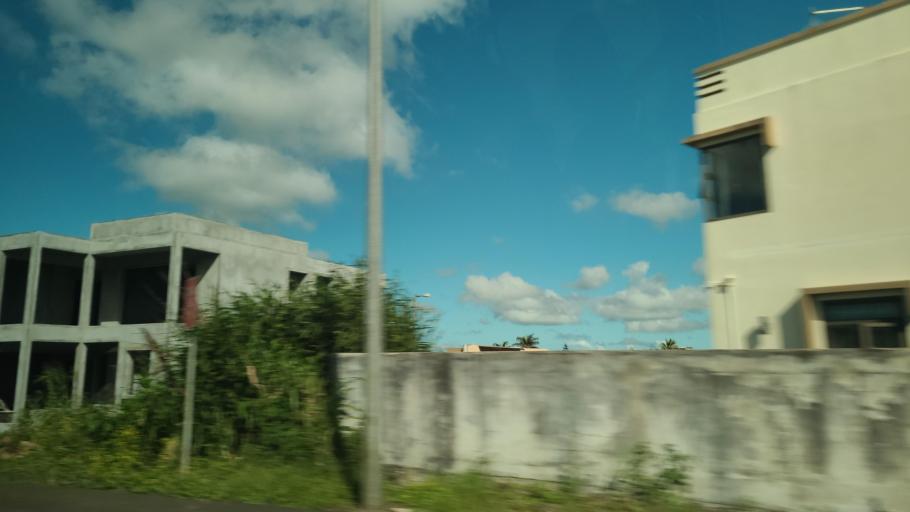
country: MU
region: Moka
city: Providence
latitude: -20.2457
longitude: 57.6111
